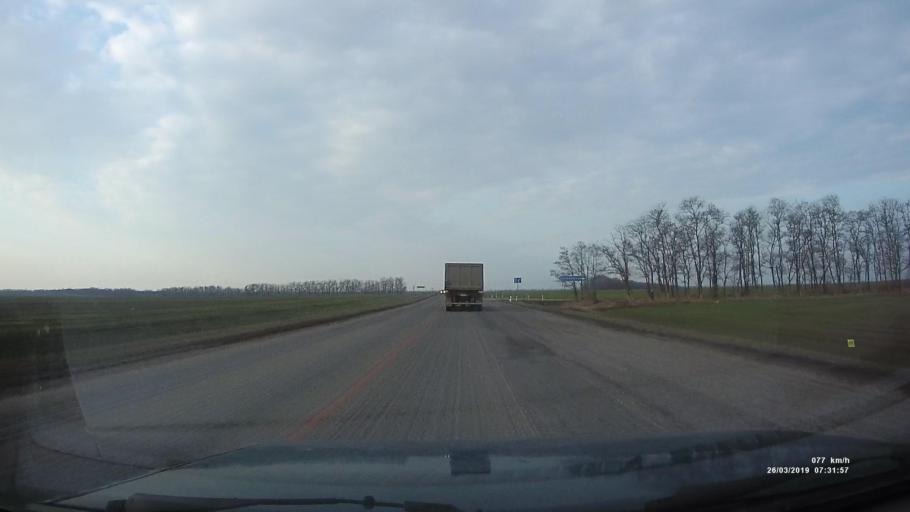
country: RU
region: Rostov
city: Novobessergenovka
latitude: 47.2294
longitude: 38.7832
